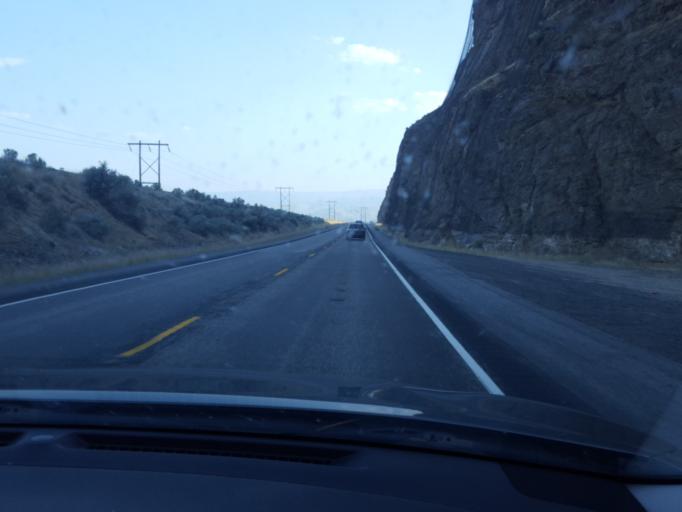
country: US
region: Washington
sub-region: Chelan County
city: Sunnyslope
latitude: 47.5116
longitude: -120.3083
